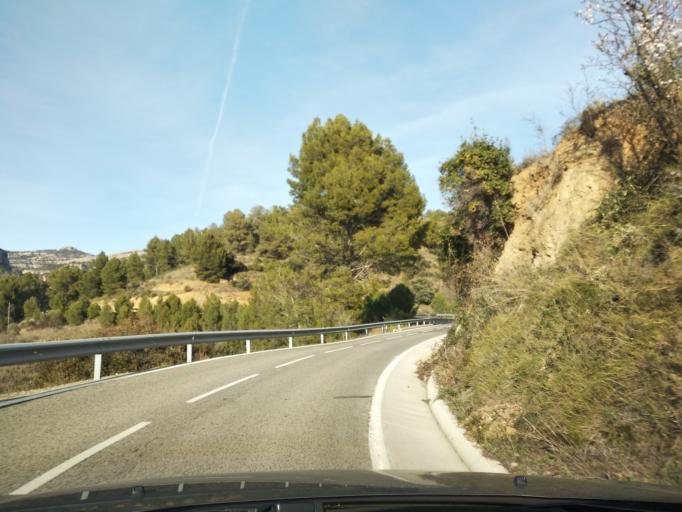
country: ES
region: Catalonia
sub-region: Provincia de Tarragona
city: Margalef
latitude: 41.2333
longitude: 0.7811
